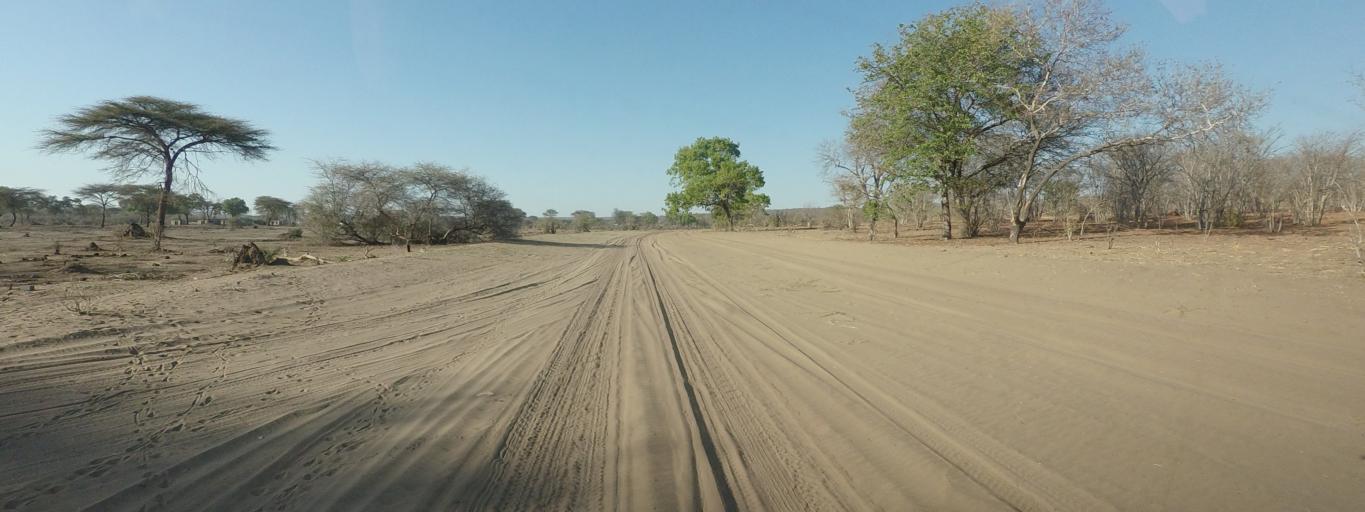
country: BW
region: North West
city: Kasane
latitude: -17.8804
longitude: 25.2340
